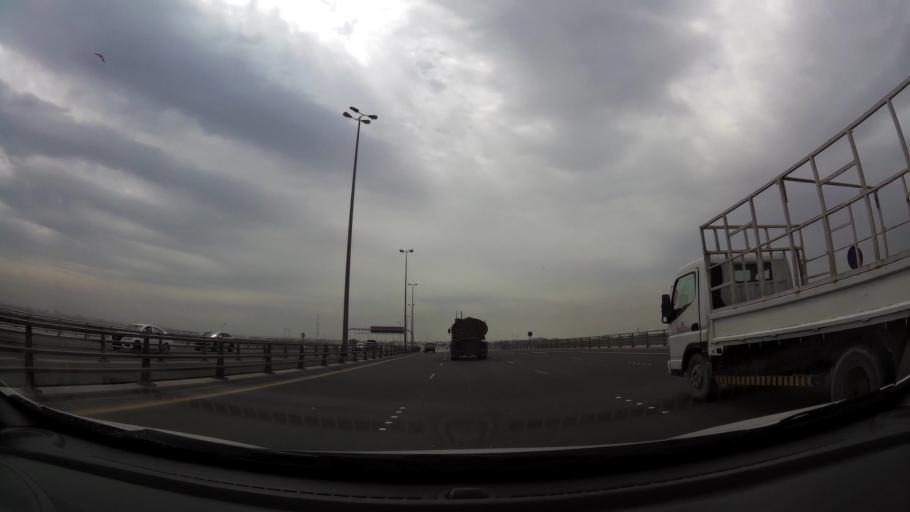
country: BH
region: Manama
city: Manama
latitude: 26.1938
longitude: 50.5888
